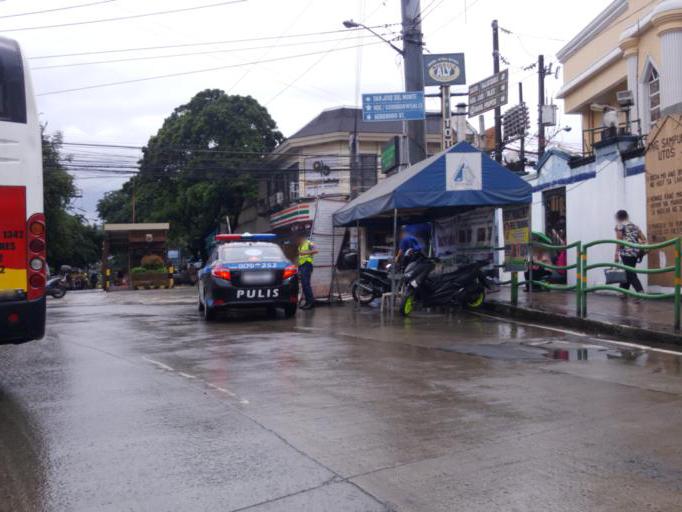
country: PH
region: Calabarzon
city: Bagong Pagasa
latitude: 14.7220
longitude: 121.0413
